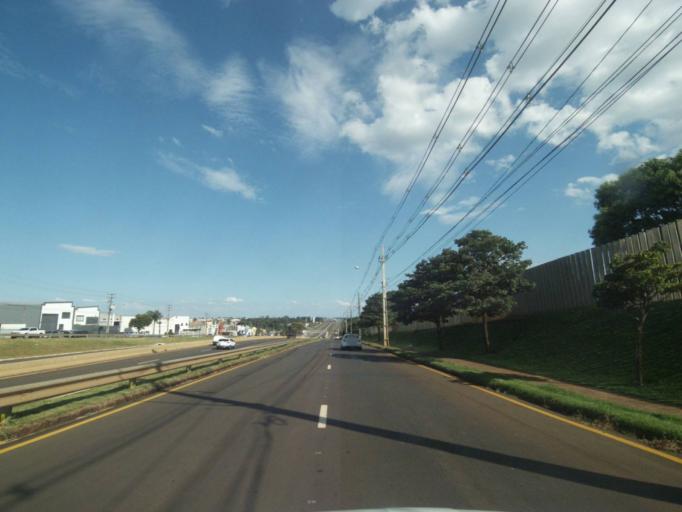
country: BR
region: Parana
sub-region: Londrina
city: Londrina
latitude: -23.3513
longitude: -51.1662
